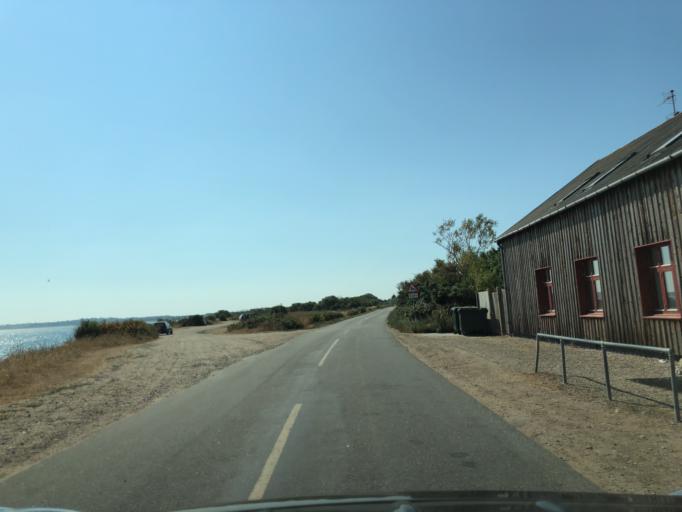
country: DK
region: Zealand
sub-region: Odsherred Kommune
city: Asnaes
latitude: 56.0013
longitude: 11.2867
